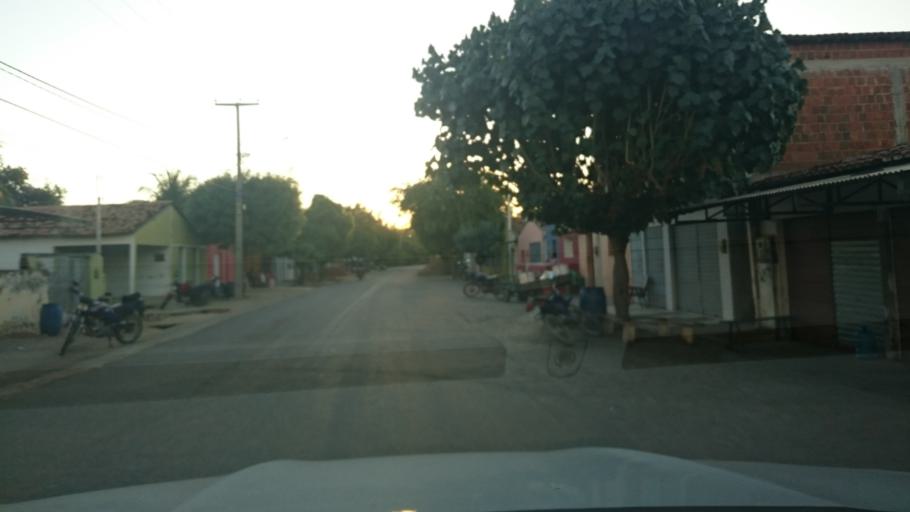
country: BR
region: Rio Grande do Norte
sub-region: Umarizal
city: Umarizal
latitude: -6.0248
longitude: -37.9907
